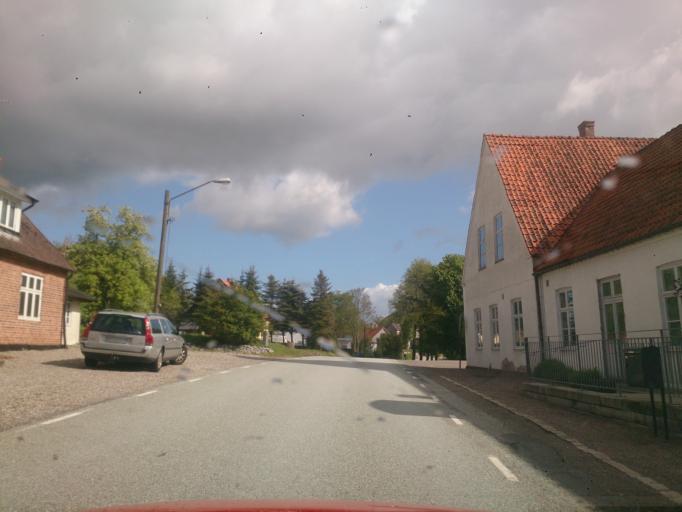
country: SE
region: Skane
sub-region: Ystads Kommun
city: Ystad
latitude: 55.4859
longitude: 13.7124
